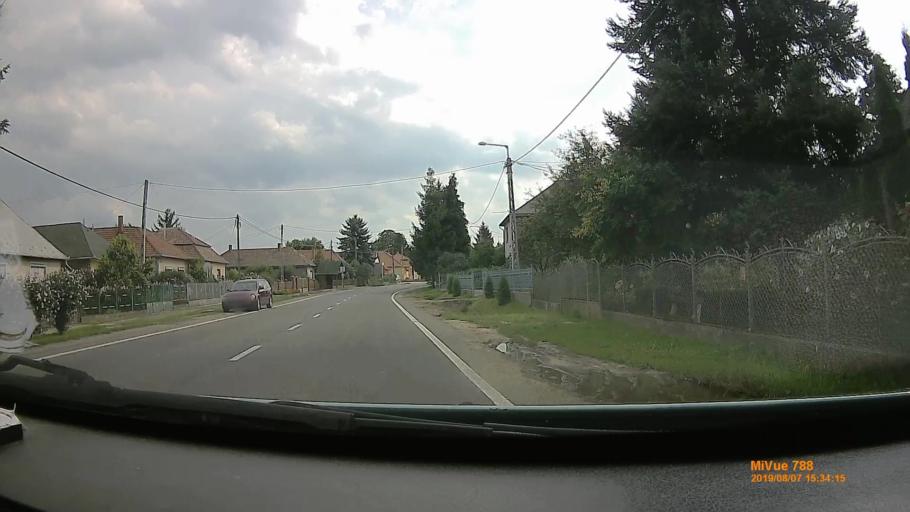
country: HU
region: Borsod-Abauj-Zemplen
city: Encs
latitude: 48.4192
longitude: 21.1746
